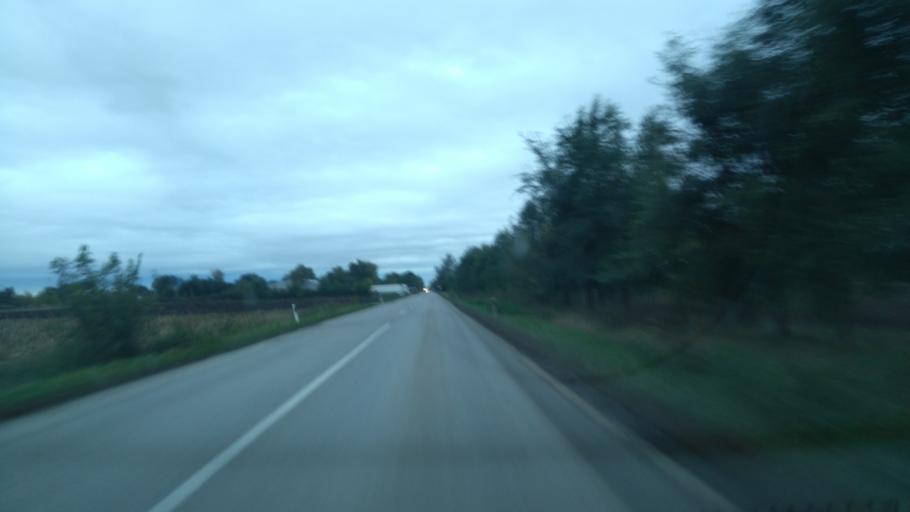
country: RS
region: Autonomna Pokrajina Vojvodina
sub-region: Juznobacki Okrug
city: Durdevo
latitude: 45.3359
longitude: 20.0610
